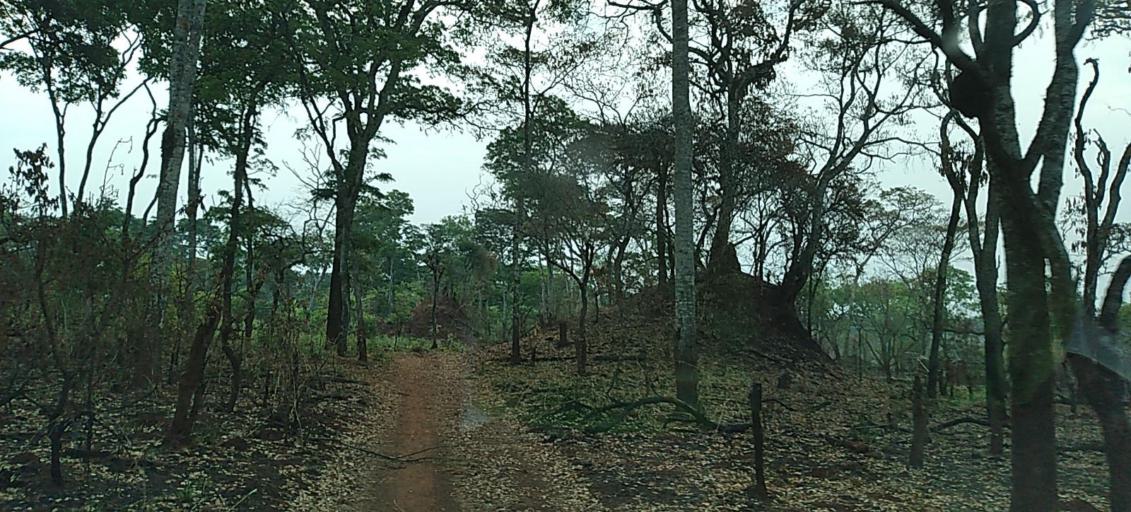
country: ZM
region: North-Western
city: Solwezi
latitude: -12.0450
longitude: 26.0101
